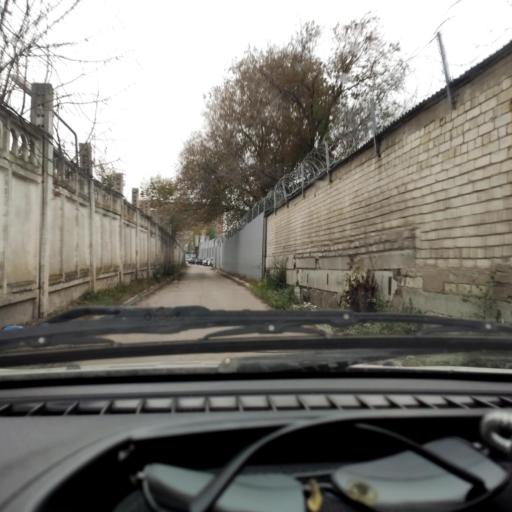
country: RU
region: Samara
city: Zhigulevsk
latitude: 53.4855
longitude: 49.4900
